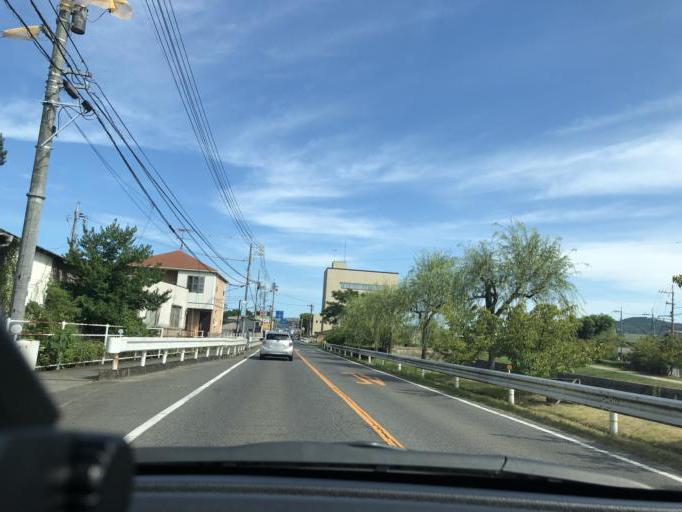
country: JP
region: Okayama
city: Kurashiki
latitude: 34.5848
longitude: 133.7790
